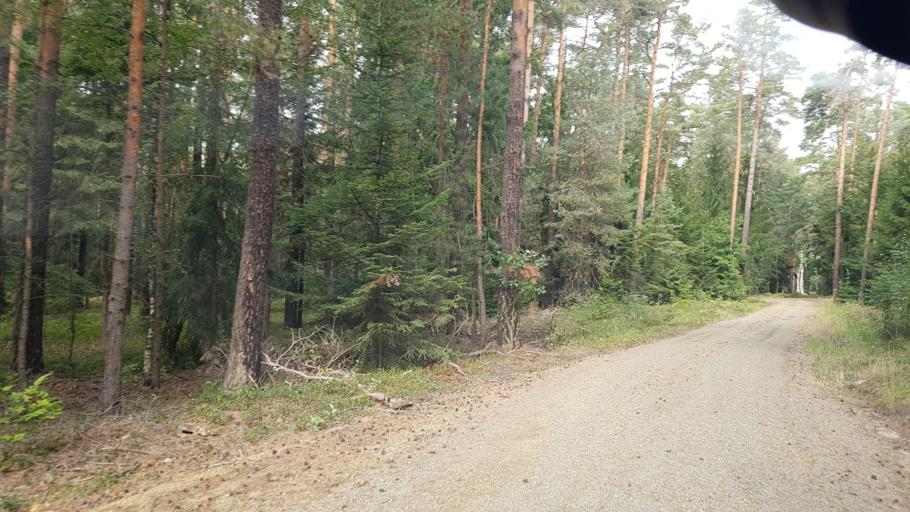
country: DE
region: Brandenburg
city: Ruckersdorf
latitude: 51.5708
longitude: 13.6295
